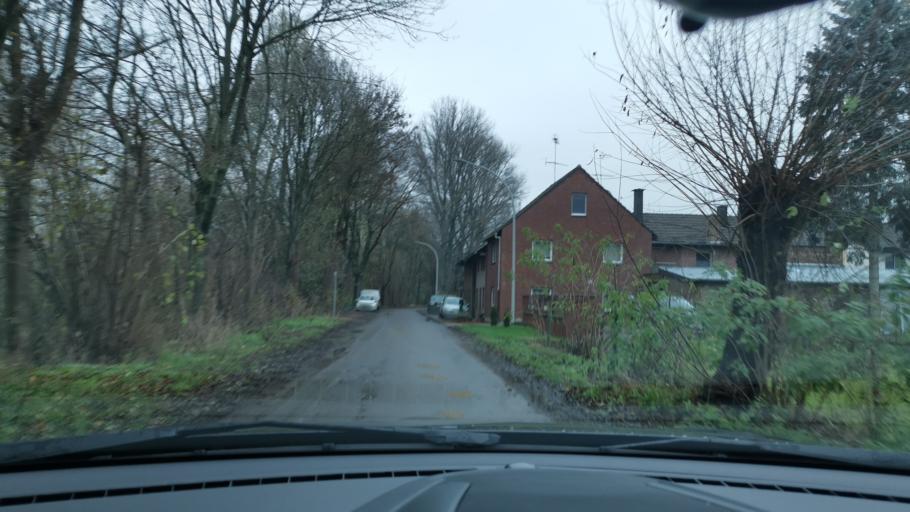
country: DE
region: North Rhine-Westphalia
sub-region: Regierungsbezirk Dusseldorf
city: Juchen
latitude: 51.1097
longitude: 6.5224
